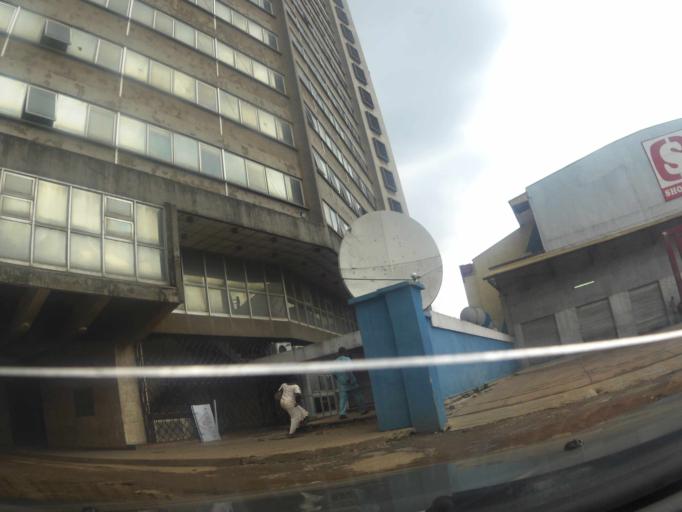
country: NG
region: Oyo
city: Ibadan
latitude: 7.3879
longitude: 3.8786
